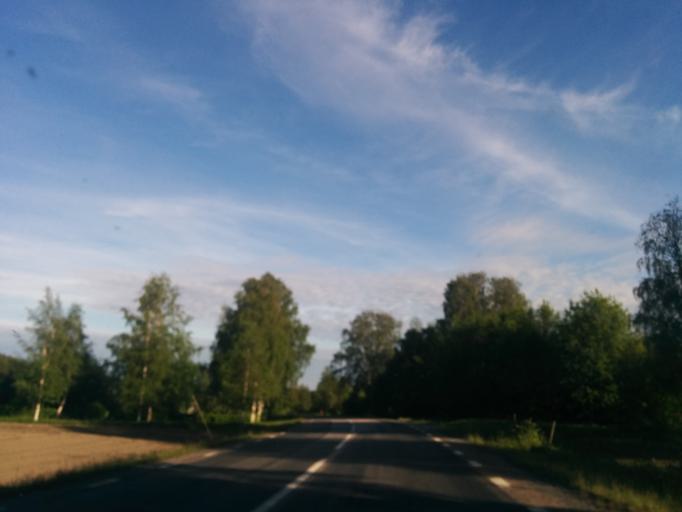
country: SE
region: Vaesternorrland
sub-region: Kramfors Kommun
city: Kramfors
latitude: 63.0039
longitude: 17.8349
